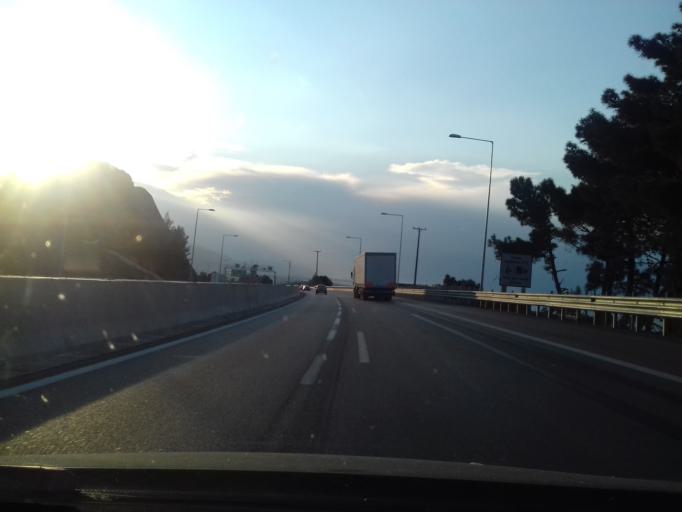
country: GR
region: West Greece
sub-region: Nomos Achaias
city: Akrata
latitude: 38.1736
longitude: 22.2572
